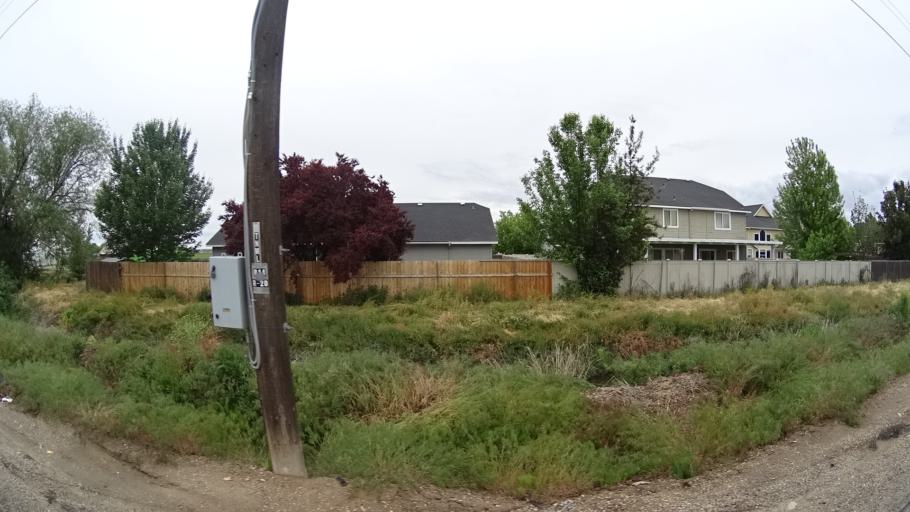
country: US
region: Idaho
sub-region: Ada County
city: Star
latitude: 43.6341
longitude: -116.4578
